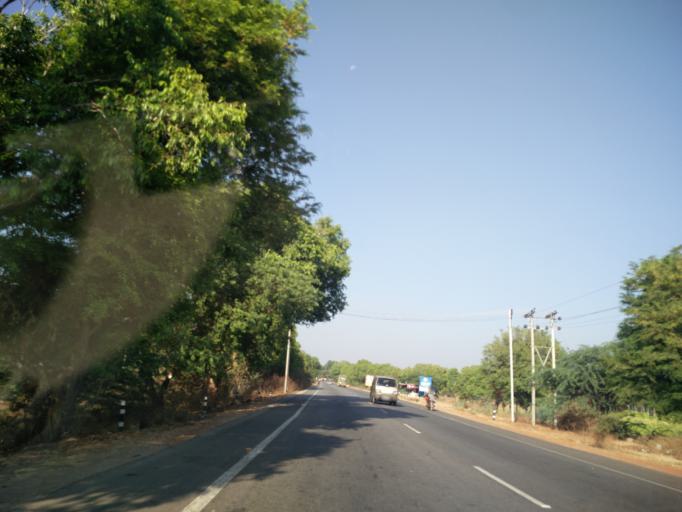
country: IN
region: Karnataka
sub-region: Tumkur
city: Gubbi
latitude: 13.3329
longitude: 76.9745
